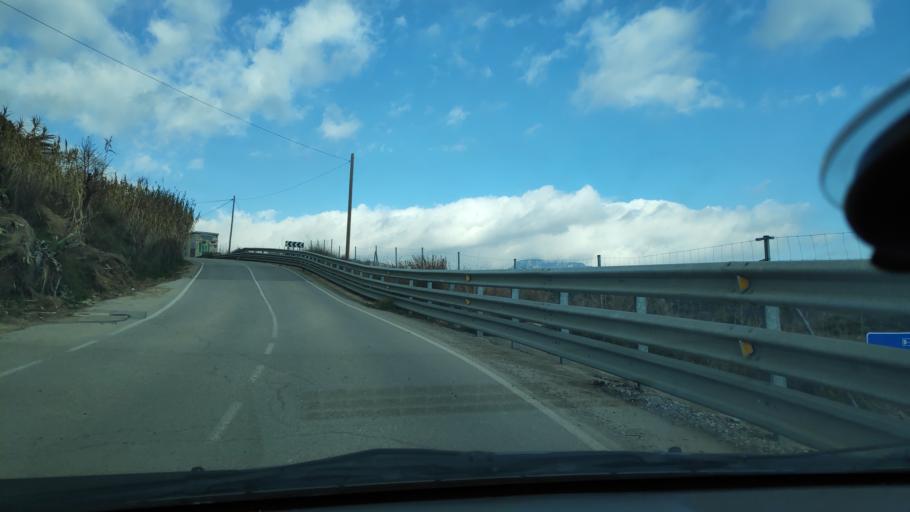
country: ES
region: Catalonia
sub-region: Provincia de Barcelona
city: Terrassa
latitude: 41.5710
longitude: 1.9898
